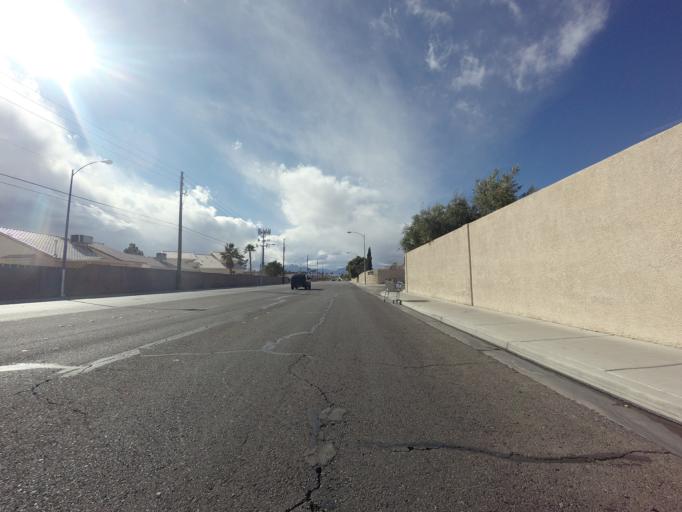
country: US
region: Nevada
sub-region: Clark County
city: North Las Vegas
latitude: 36.2544
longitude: -115.1504
